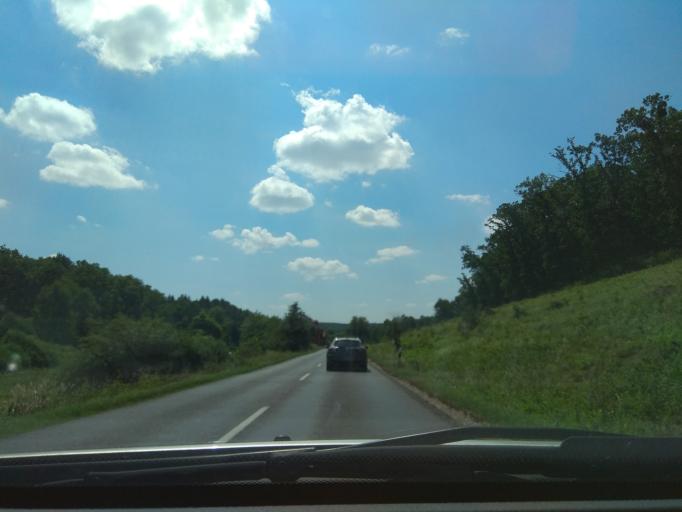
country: HU
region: Borsod-Abauj-Zemplen
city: Harsany
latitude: 48.0067
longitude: 20.7620
